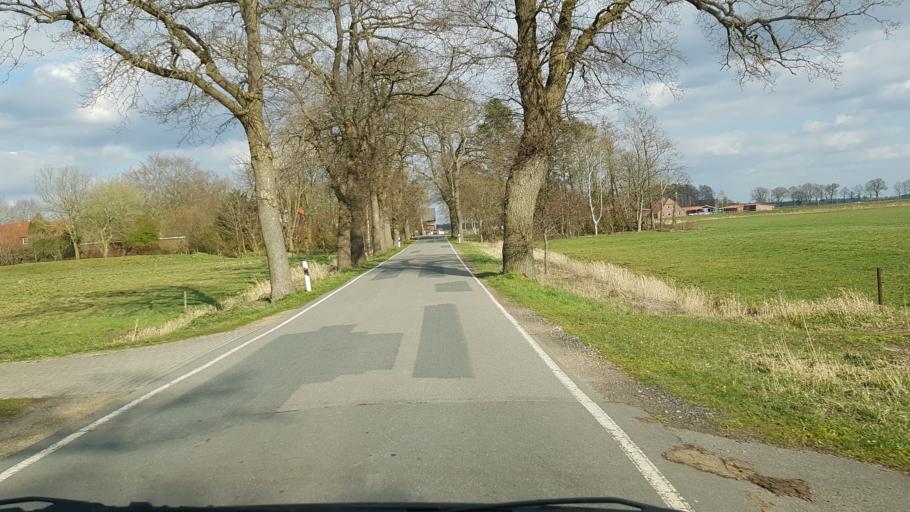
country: DE
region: Lower Saxony
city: Rastede
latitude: 53.2850
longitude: 8.2751
